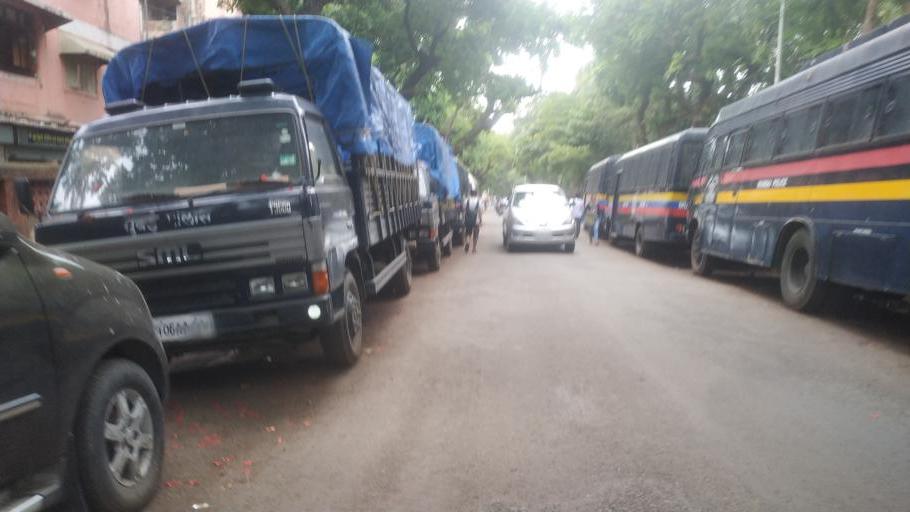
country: IN
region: Maharashtra
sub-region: Mumbai Suburban
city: Mumbai
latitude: 19.0090
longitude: 72.8472
